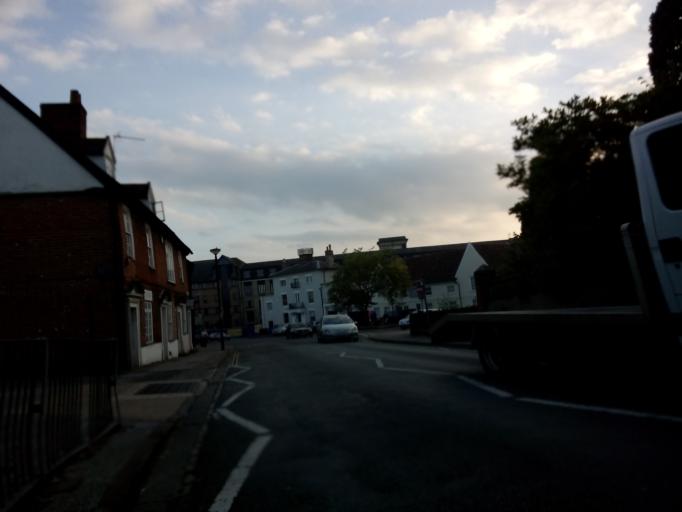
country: GB
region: England
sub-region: Suffolk
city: Ipswich
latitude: 52.0596
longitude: 1.1591
